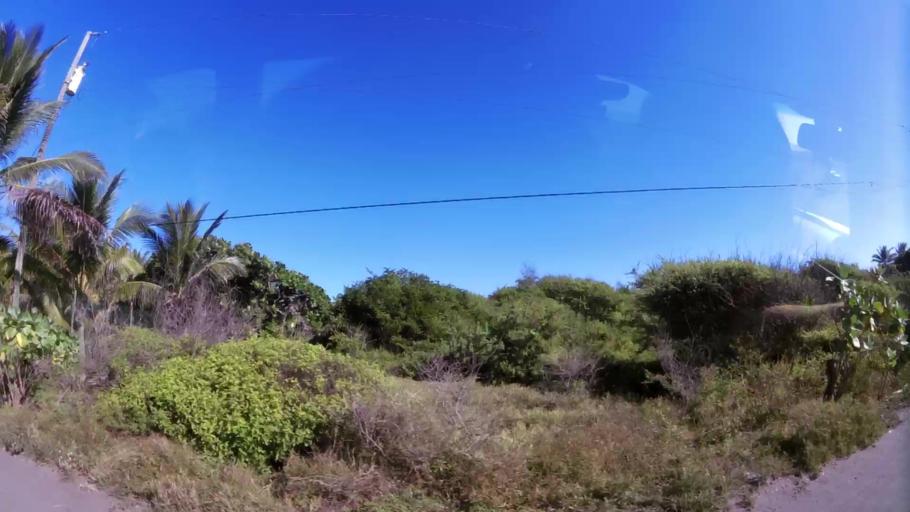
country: GT
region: Jutiapa
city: Pasaco
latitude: 13.8527
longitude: -90.3814
